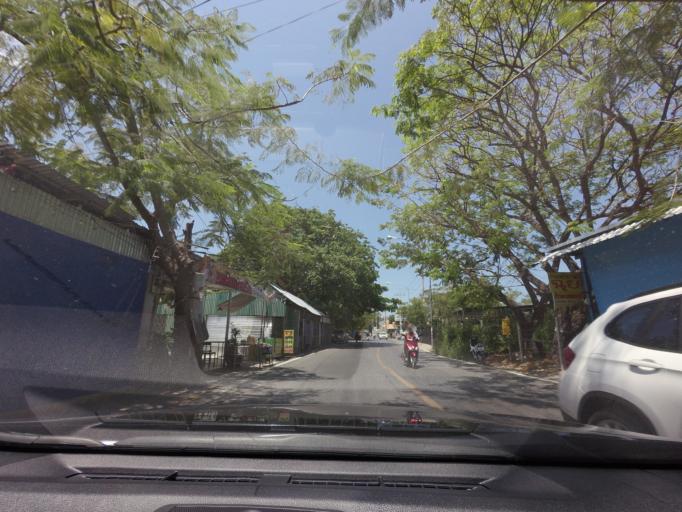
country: TH
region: Prachuap Khiri Khan
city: Hua Hin
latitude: 12.5657
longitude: 99.9552
